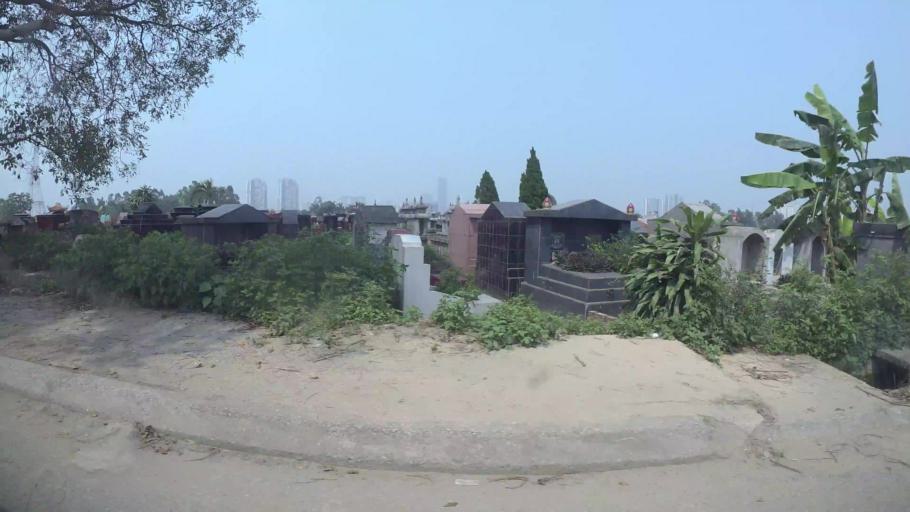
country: VN
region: Ha Noi
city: Ha Dong
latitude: 20.9935
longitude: 105.7668
